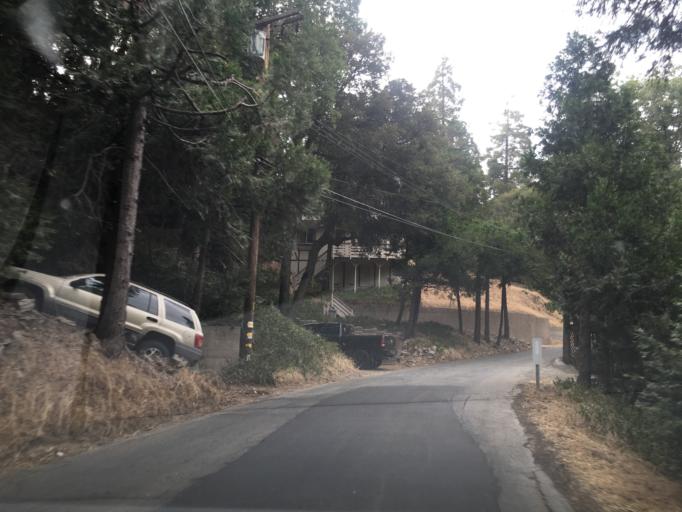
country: US
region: California
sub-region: San Bernardino County
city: Crestline
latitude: 34.2466
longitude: -117.2742
